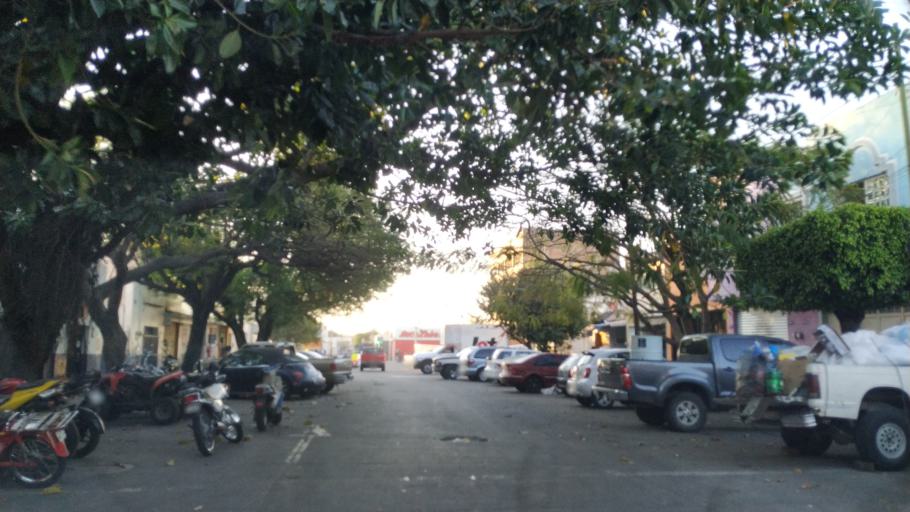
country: MX
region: Jalisco
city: Tlaquepaque
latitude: 20.6544
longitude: -103.3354
